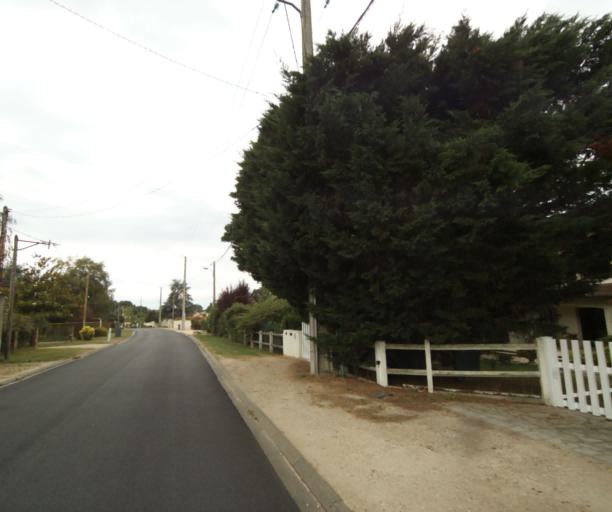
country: FR
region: Ile-de-France
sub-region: Departement de Seine-et-Marne
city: Saint-Sauveur-sur-Ecole
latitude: 48.4881
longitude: 2.5385
